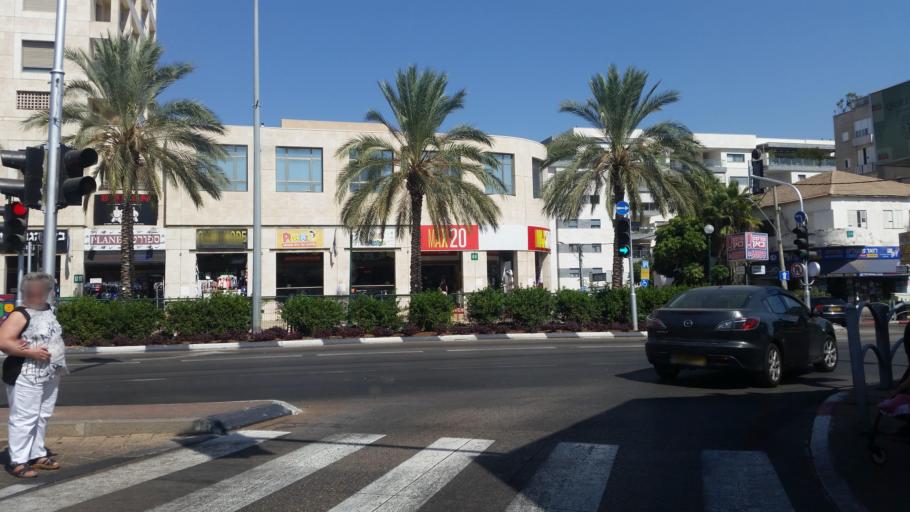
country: IL
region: Central District
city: Ra'anana
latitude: 32.1795
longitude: 34.8784
